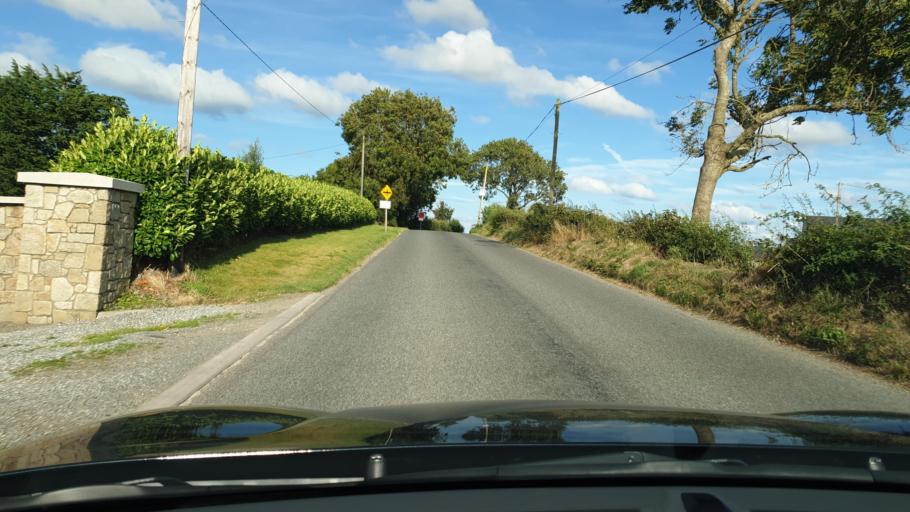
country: IE
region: Leinster
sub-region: An Mhi
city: Duleek
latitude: 53.6248
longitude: -6.3489
